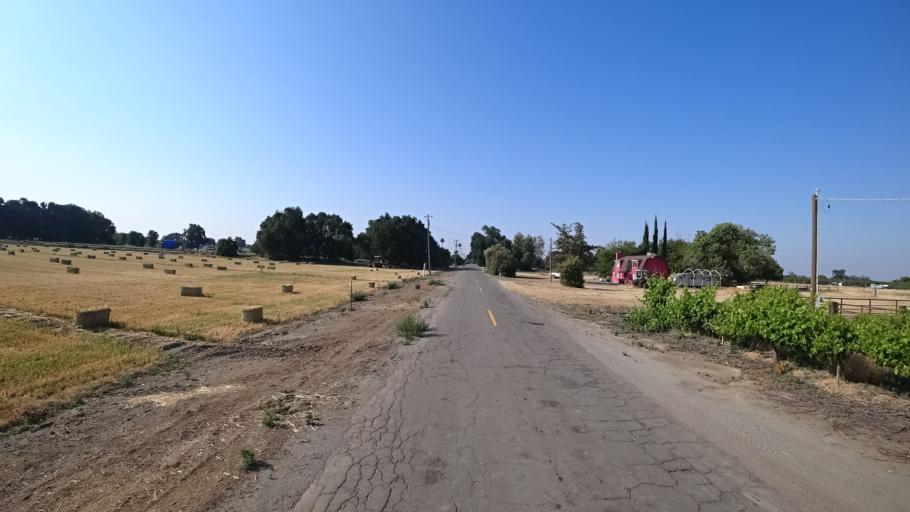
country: US
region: California
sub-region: Fresno County
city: Riverdale
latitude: 36.3713
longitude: -119.8252
